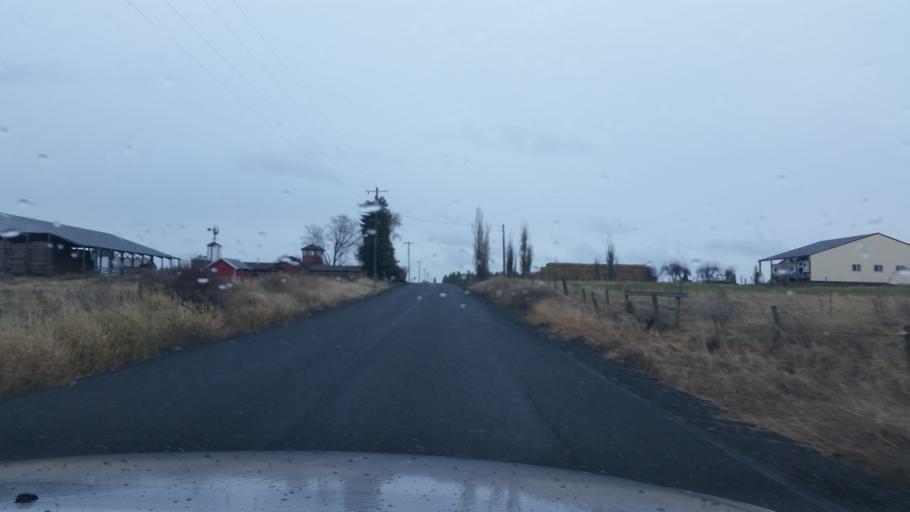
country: US
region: Washington
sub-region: Spokane County
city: Medical Lake
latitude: 47.6143
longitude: -117.7478
